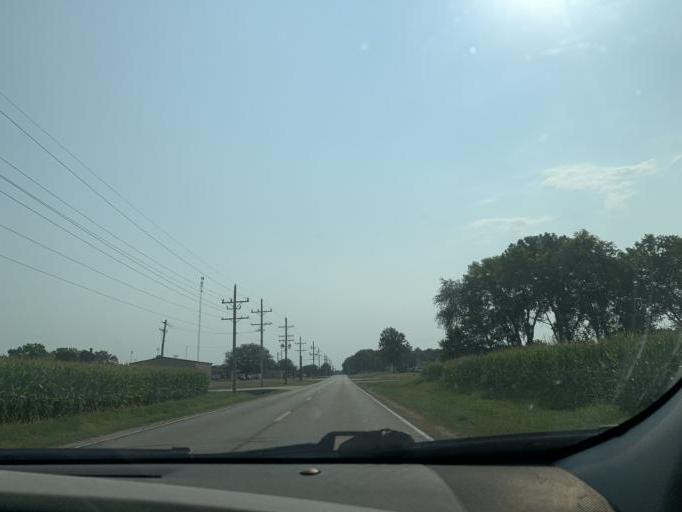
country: US
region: Illinois
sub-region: Whiteside County
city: Sterling
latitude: 41.8013
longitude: -89.7385
